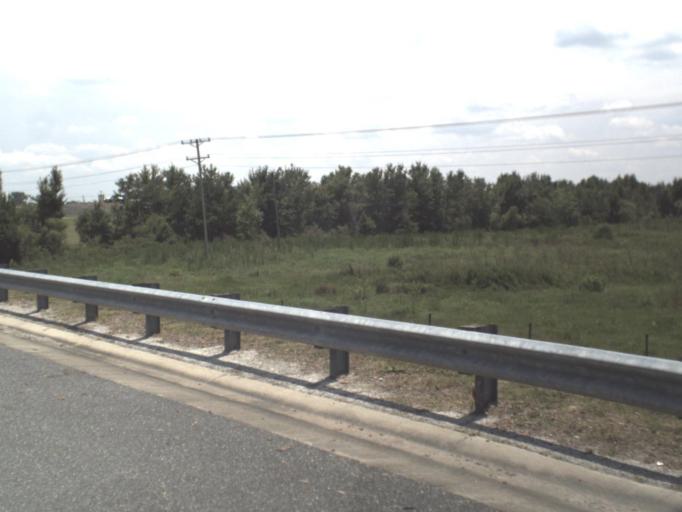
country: US
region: Florida
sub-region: Bradford County
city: Starke
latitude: 30.0677
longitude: -82.1846
